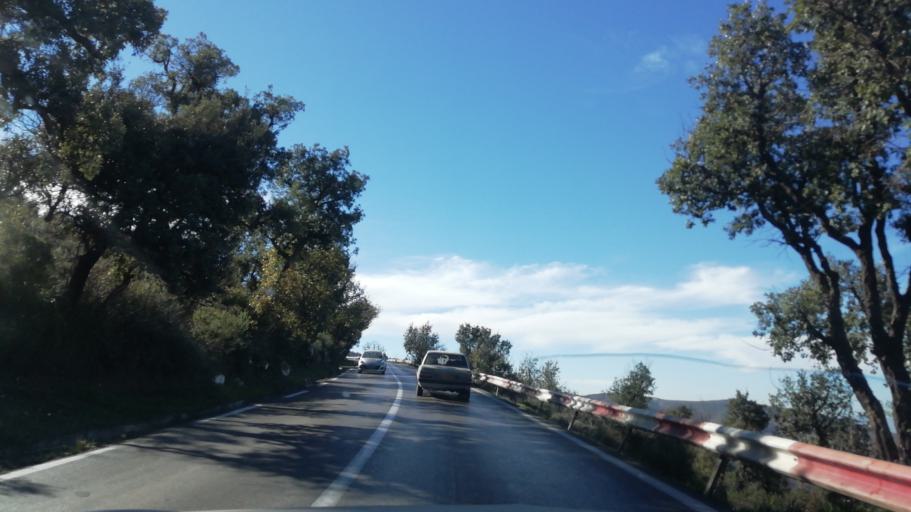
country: DZ
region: Tlemcen
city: Mansoura
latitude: 34.8428
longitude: -1.3660
